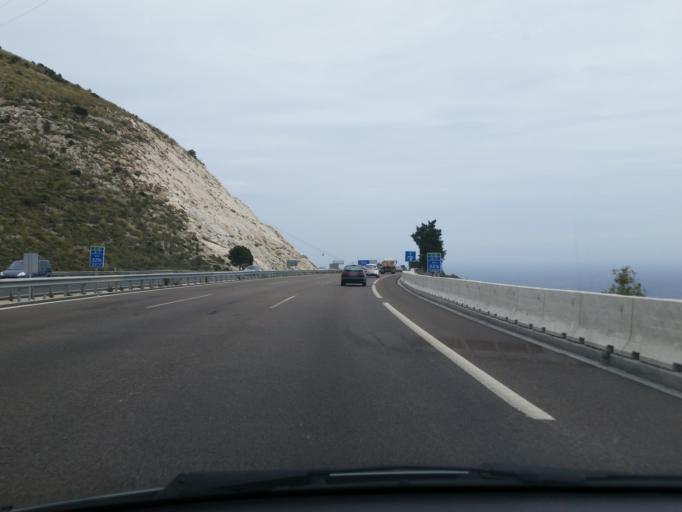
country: ES
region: Andalusia
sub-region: Provincia de Malaga
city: Benalmadena
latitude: 36.6065
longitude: -4.5542
